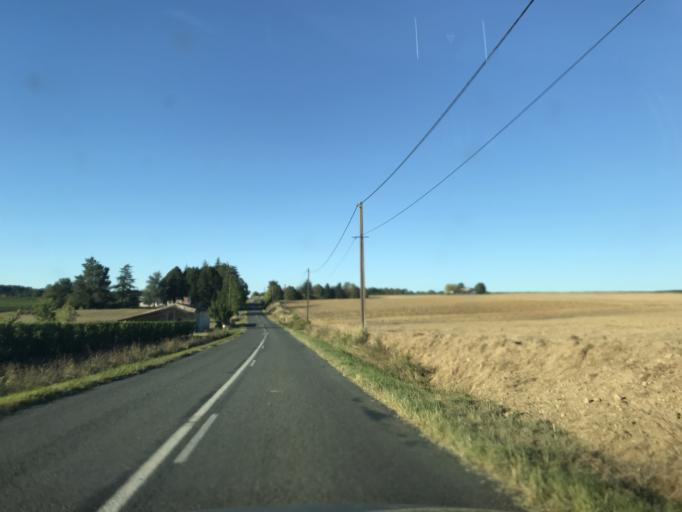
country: FR
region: Aquitaine
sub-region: Departement de la Gironde
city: Sauveterre-de-Guyenne
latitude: 44.7072
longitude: -0.0671
